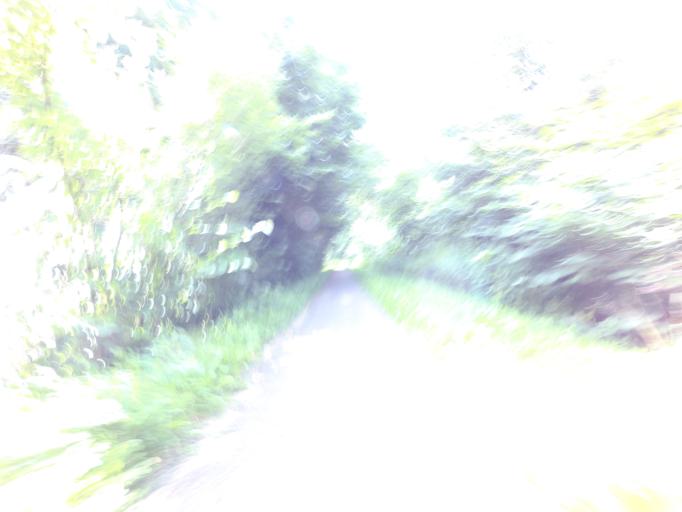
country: DK
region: Central Jutland
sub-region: Horsens Kommune
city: Horsens
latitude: 55.9312
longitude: 9.7701
